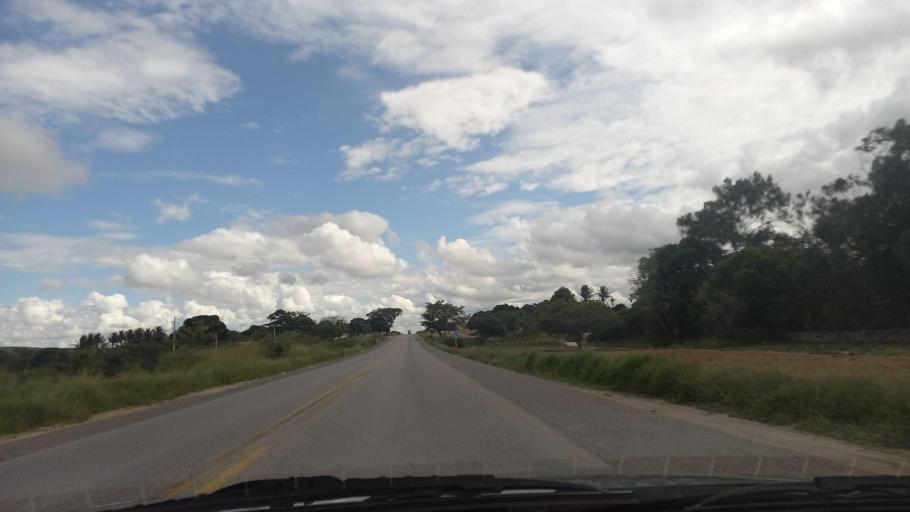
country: BR
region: Pernambuco
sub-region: Lajedo
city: Lajedo
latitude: -8.6795
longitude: -36.4044
